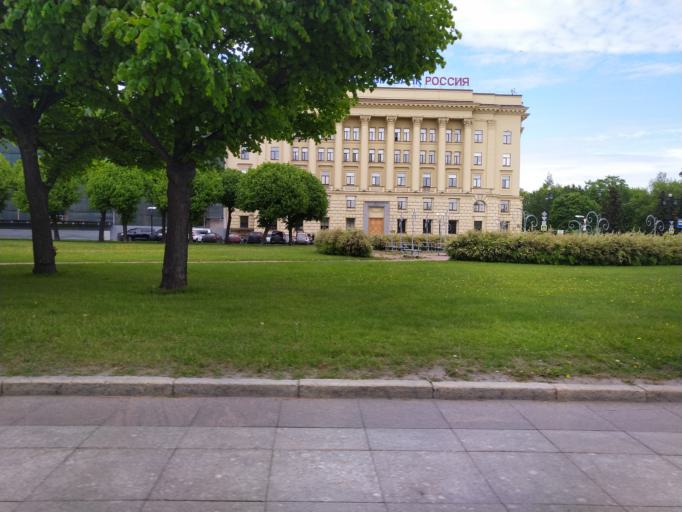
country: RU
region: Leningrad
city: Finlyandskiy
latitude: 59.9487
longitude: 30.3897
